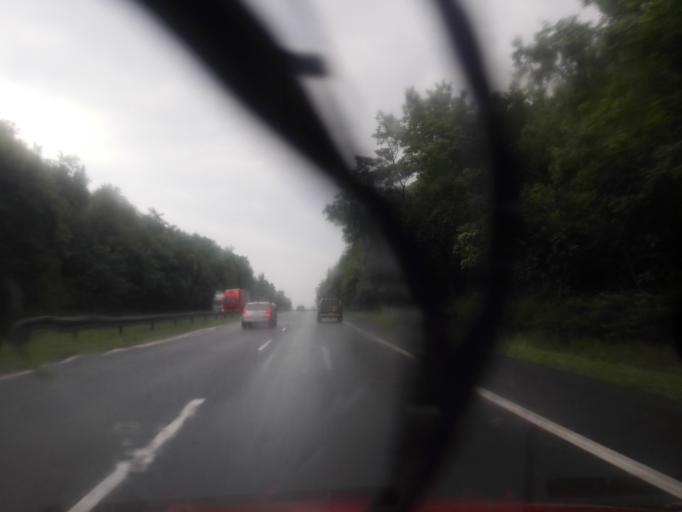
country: PL
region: Silesian Voivodeship
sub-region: Czestochowa
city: Czestochowa
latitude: 50.8396
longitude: 19.1475
